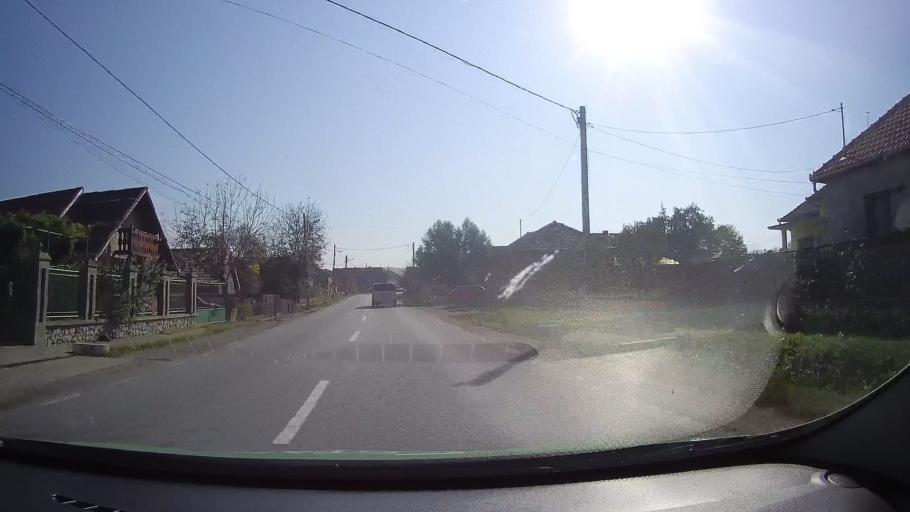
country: RO
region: Hunedoara
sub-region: Comuna Dobra
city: Dobra
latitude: 45.9164
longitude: 22.5619
